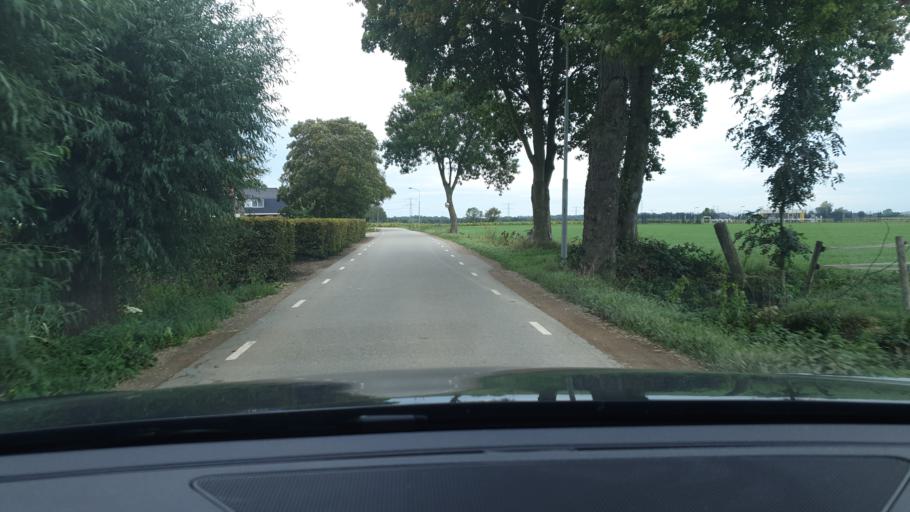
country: NL
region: Gelderland
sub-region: Gemeente Overbetuwe
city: Oosterhout
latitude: 51.8979
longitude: 5.8215
